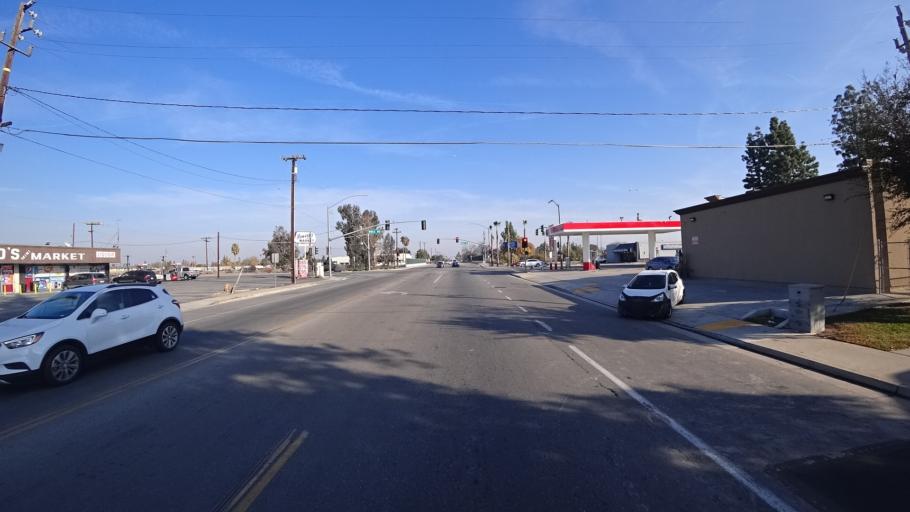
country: US
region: California
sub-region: Kern County
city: Bakersfield
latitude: 35.3250
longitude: -119.0397
